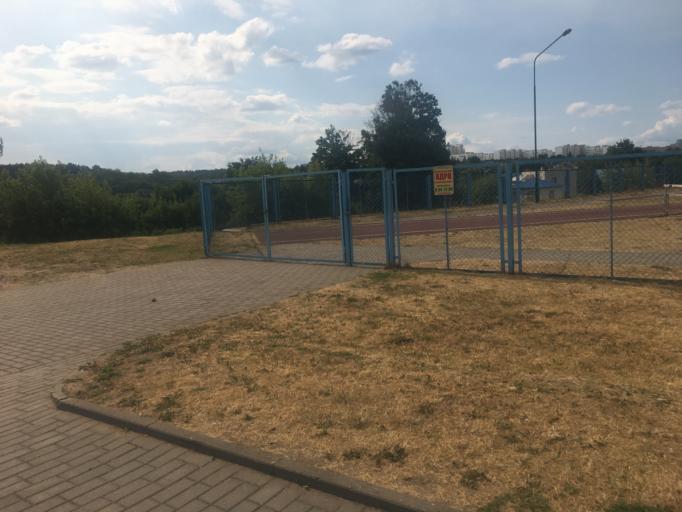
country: BY
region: Grodnenskaya
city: Hrodna
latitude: 53.6821
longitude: 23.8152
